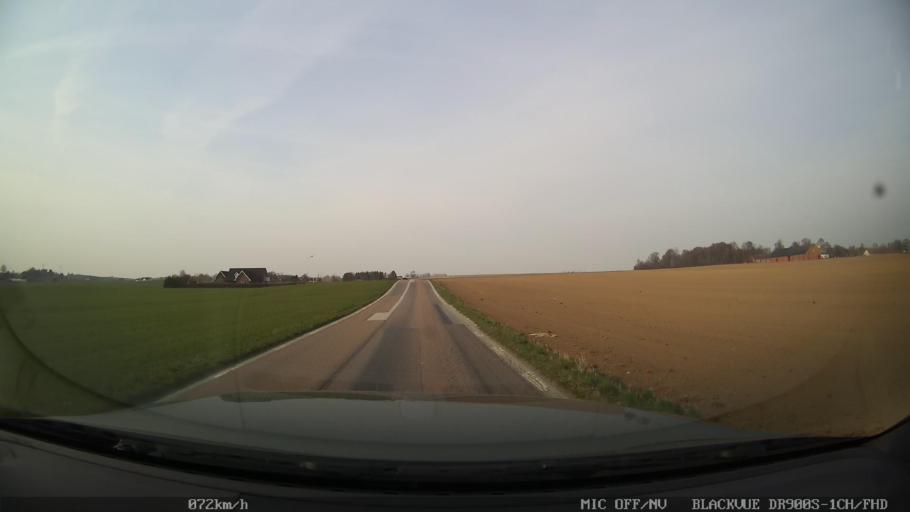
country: SE
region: Skane
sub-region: Ystads Kommun
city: Ystad
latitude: 55.4497
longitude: 13.8315
